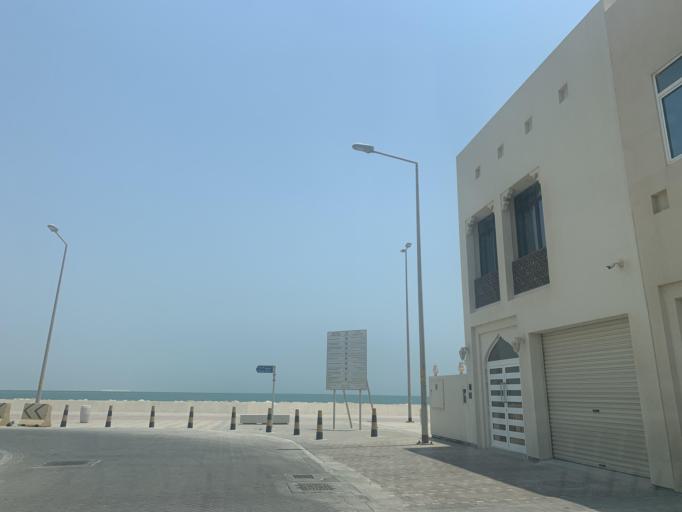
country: BH
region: Muharraq
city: Al Hadd
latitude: 26.2397
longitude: 50.6742
